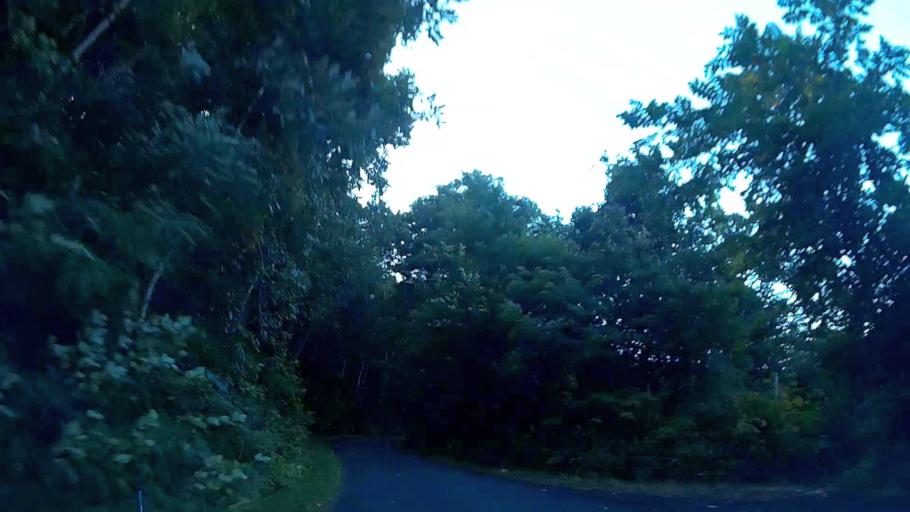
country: JP
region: Hokkaido
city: Iwanai
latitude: 42.6464
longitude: 140.0376
